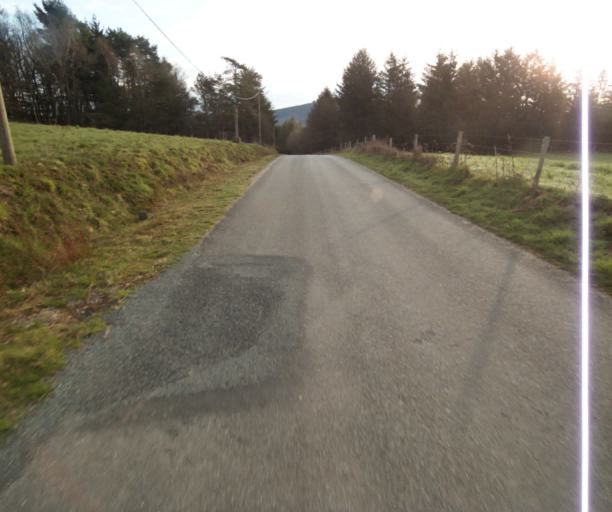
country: FR
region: Limousin
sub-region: Departement de la Correze
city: Correze
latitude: 45.4081
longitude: 1.9118
